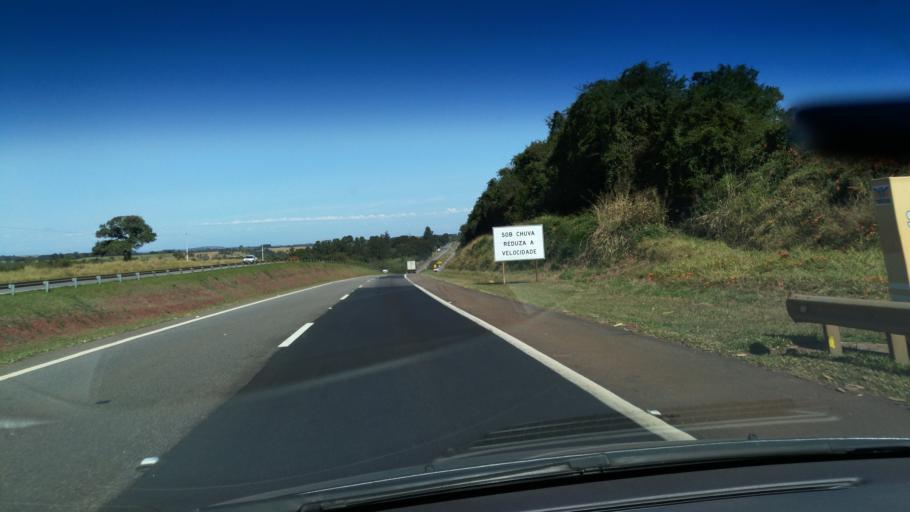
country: BR
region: Sao Paulo
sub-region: Santo Antonio De Posse
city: Santo Antonio de Posse
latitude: -22.5528
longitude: -46.9989
